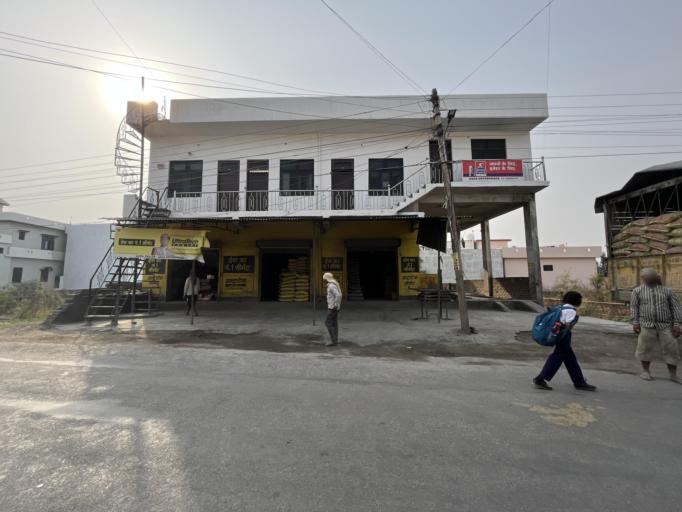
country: IN
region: Uttarakhand
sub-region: Naini Tal
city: Haldwani
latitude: 29.2060
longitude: 79.4850
